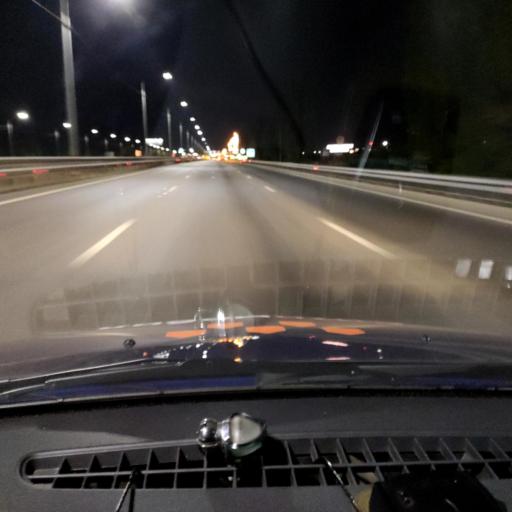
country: RU
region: Voronezj
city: Podgornoye
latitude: 51.7788
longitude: 39.1964
